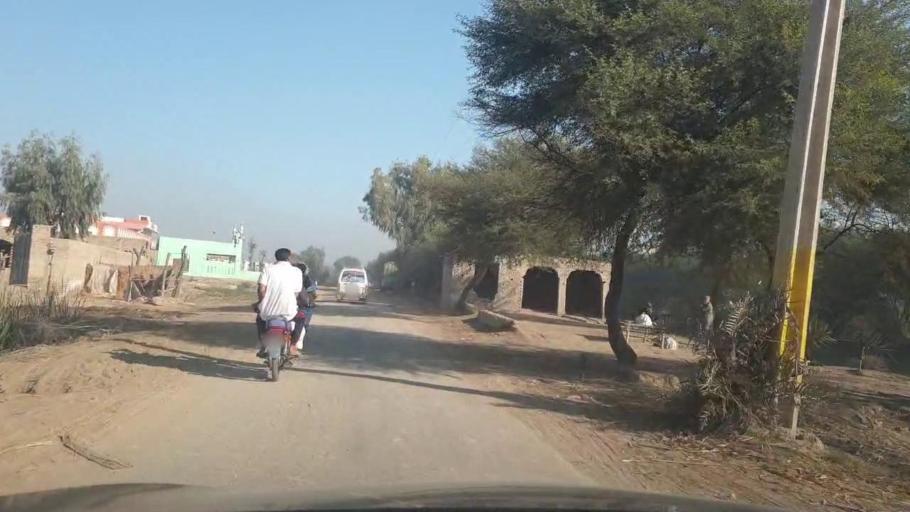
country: PK
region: Sindh
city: Mirpur Mathelo
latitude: 28.0722
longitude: 69.4674
